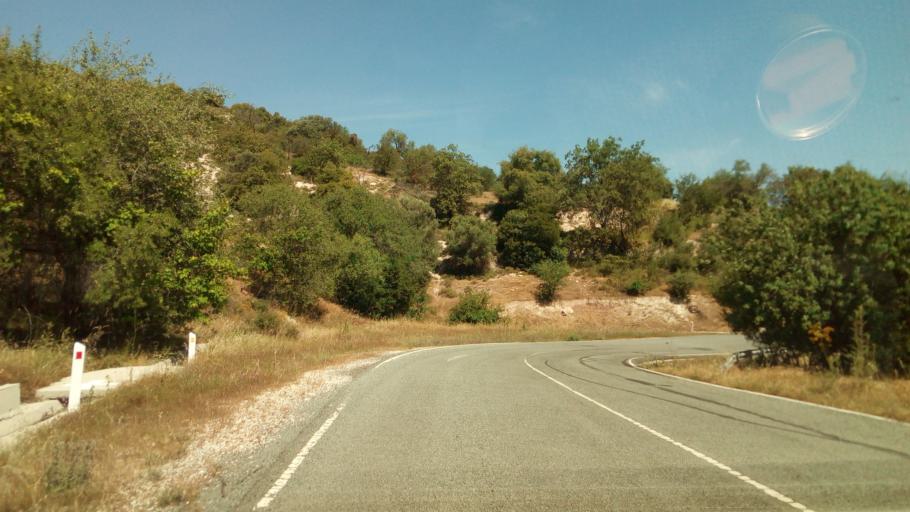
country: CY
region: Limassol
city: Pachna
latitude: 34.8120
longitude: 32.6816
